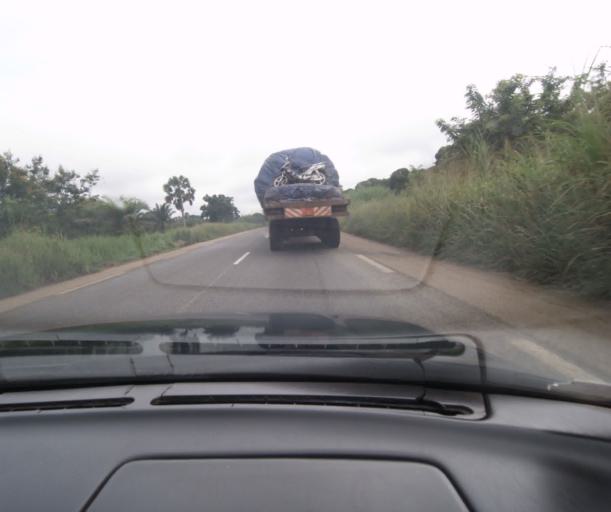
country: CM
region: Centre
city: Ombesa
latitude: 4.5858
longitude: 11.2647
